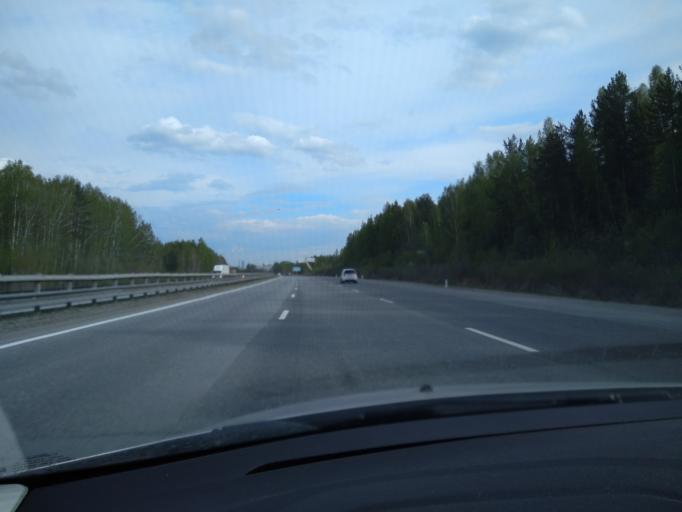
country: RU
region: Sverdlovsk
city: Shuvakish
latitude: 56.9051
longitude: 60.5134
